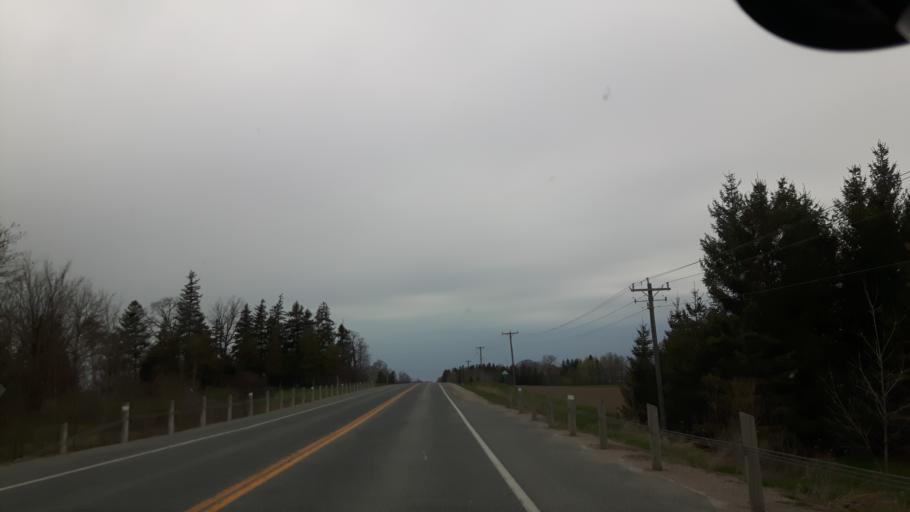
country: CA
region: Ontario
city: Bluewater
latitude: 43.6241
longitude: -81.5558
